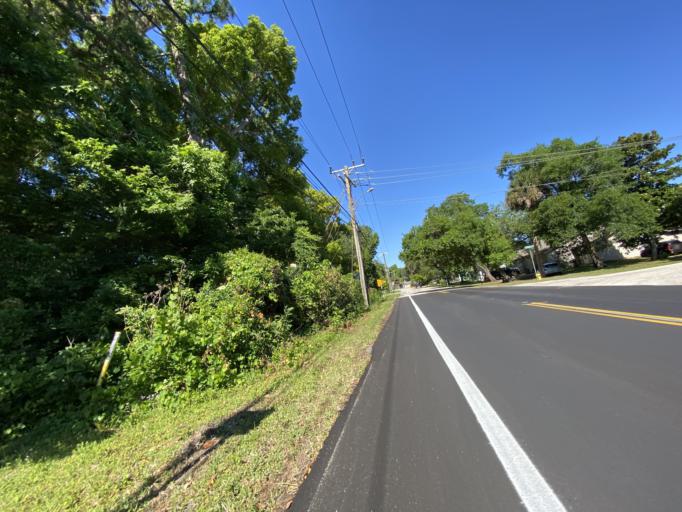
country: US
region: Florida
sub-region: Volusia County
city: Port Orange
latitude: 29.1432
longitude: -80.9987
